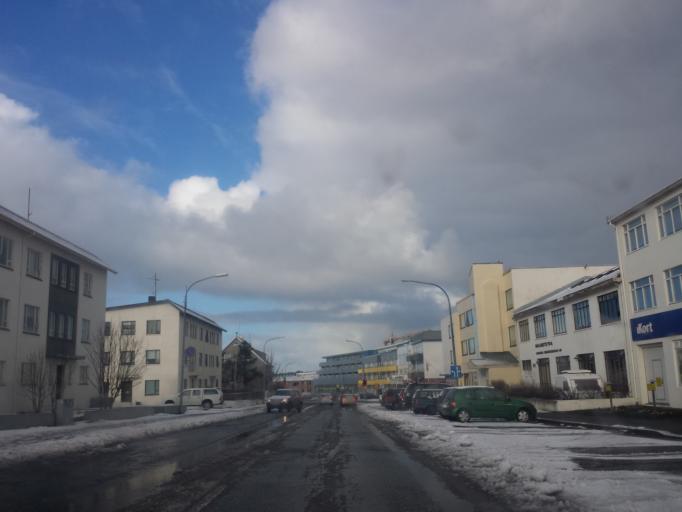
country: IS
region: Capital Region
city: Reykjavik
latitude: 64.1406
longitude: -21.9035
